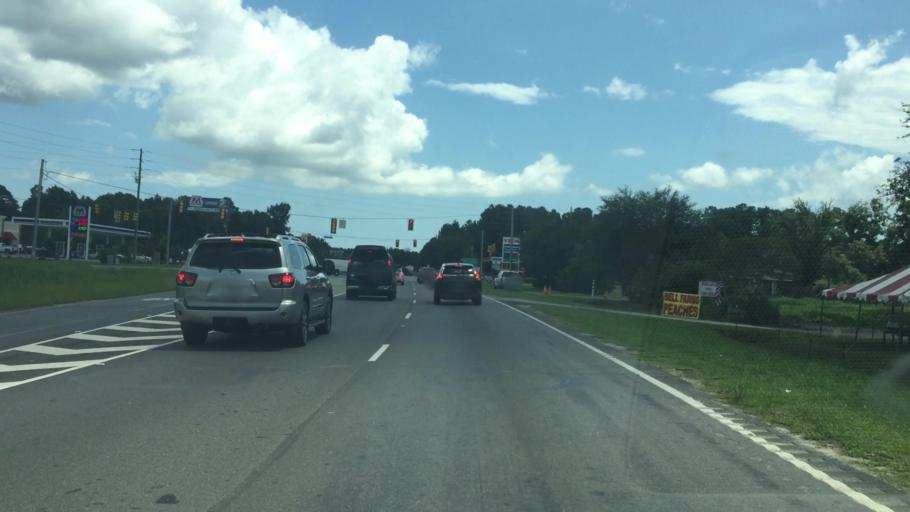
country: US
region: South Carolina
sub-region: Horry County
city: North Myrtle Beach
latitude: 33.9396
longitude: -78.7342
